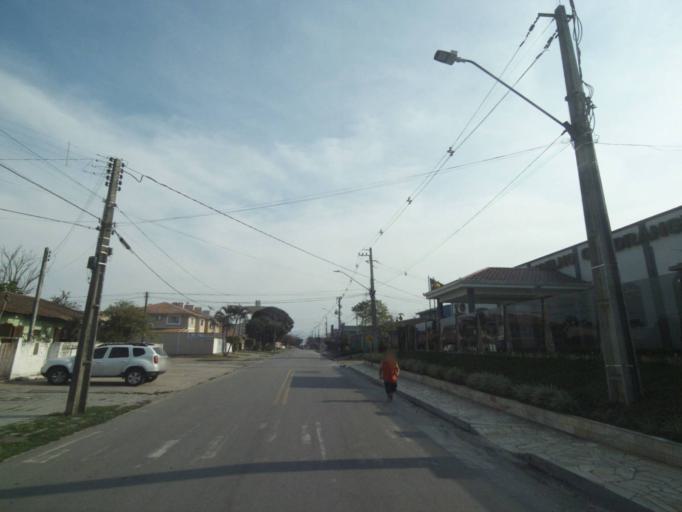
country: BR
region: Parana
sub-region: Paranagua
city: Paranagua
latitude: -25.5208
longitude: -48.5294
